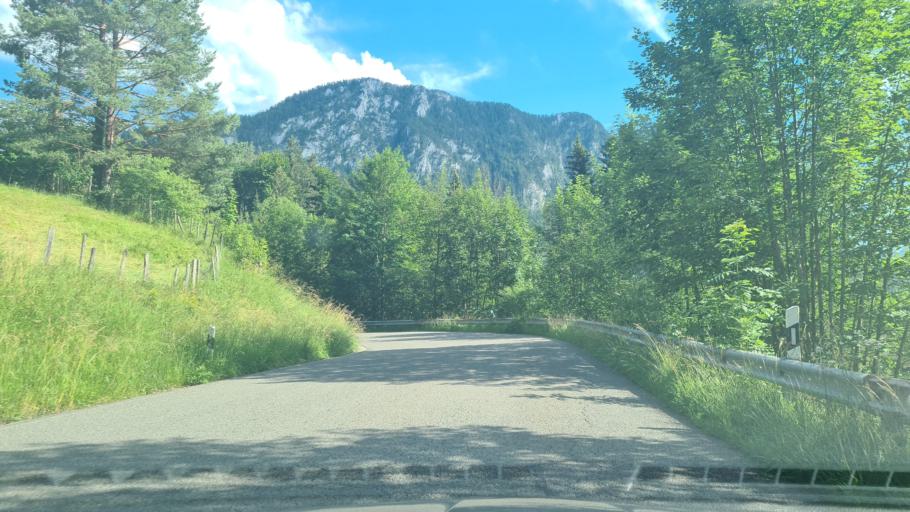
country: AT
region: Salzburg
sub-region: Politischer Bezirk Zell am See
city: Unken
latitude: 47.6692
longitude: 12.7551
